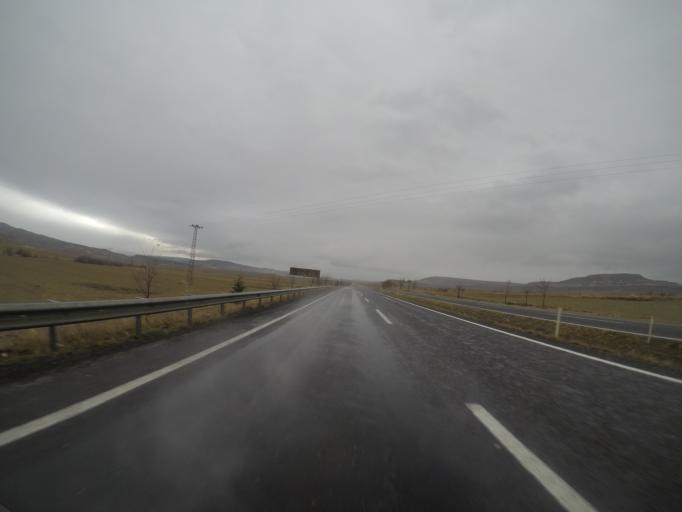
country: TR
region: Nevsehir
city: Urgub
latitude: 38.7191
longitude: 34.9429
